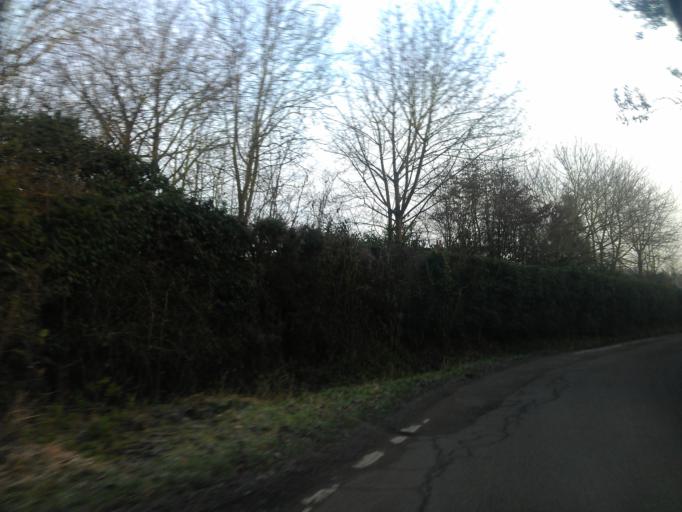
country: GB
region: England
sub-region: Essex
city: Wivenhoe
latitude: 51.8688
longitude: 0.9795
